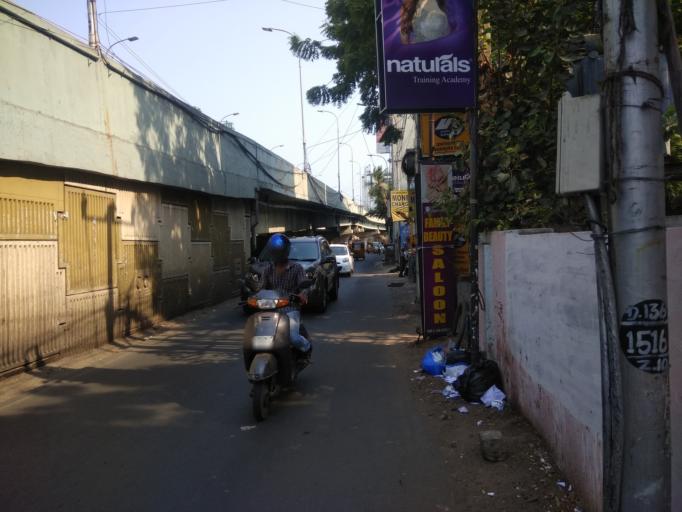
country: IN
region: Tamil Nadu
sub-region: Chennai
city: Chetput
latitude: 13.0433
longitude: 80.2323
